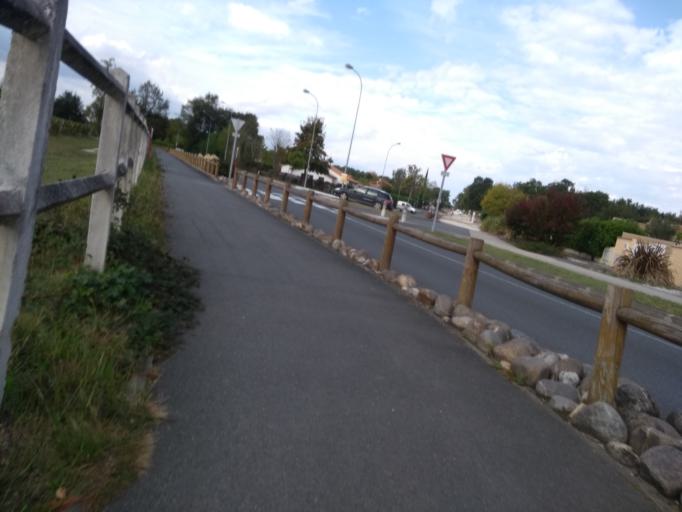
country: FR
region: Aquitaine
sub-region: Departement de la Gironde
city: Canejan
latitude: 44.7634
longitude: -0.6583
